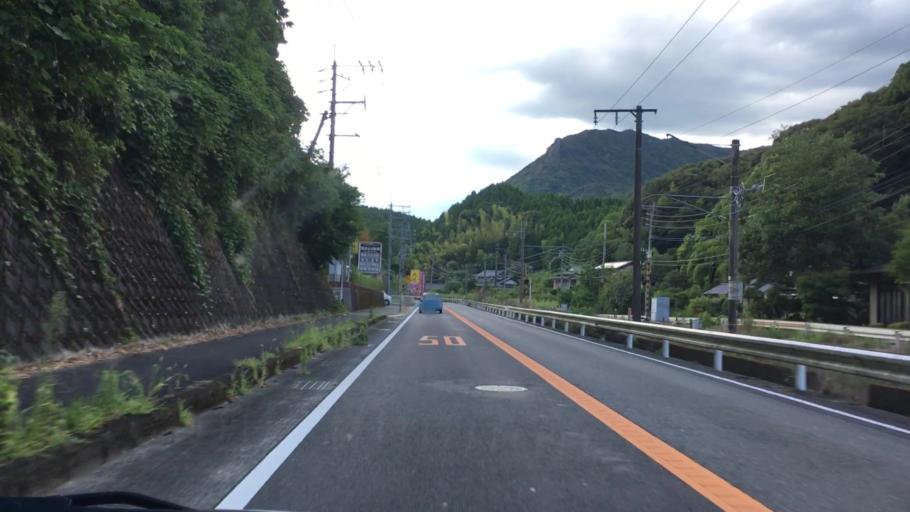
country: JP
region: Saga Prefecture
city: Imaricho-ko
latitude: 33.1914
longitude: 129.9200
